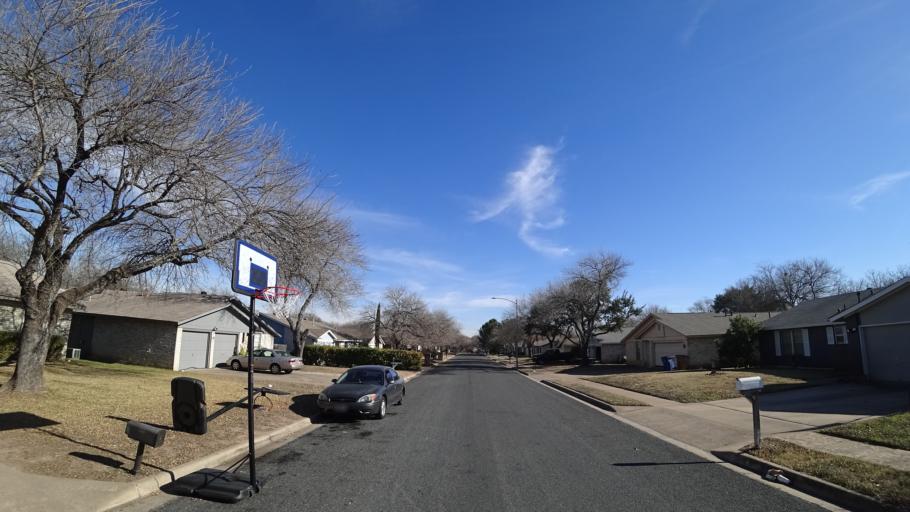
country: US
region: Texas
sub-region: Travis County
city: Wells Branch
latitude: 30.3889
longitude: -97.7026
